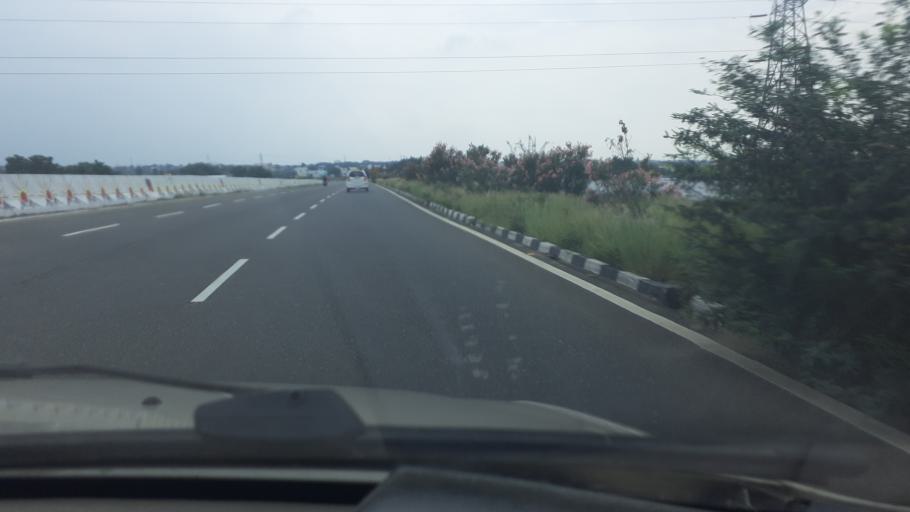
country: IN
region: Tamil Nadu
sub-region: Madurai
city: Tirupparangunram
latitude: 9.8044
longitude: 77.9840
